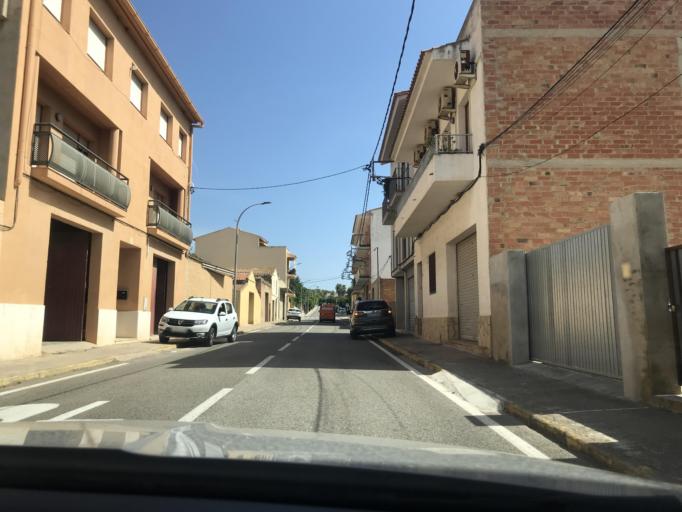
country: ES
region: Catalonia
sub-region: Provincia de Tarragona
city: Altafulla
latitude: 41.1830
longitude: 1.3761
